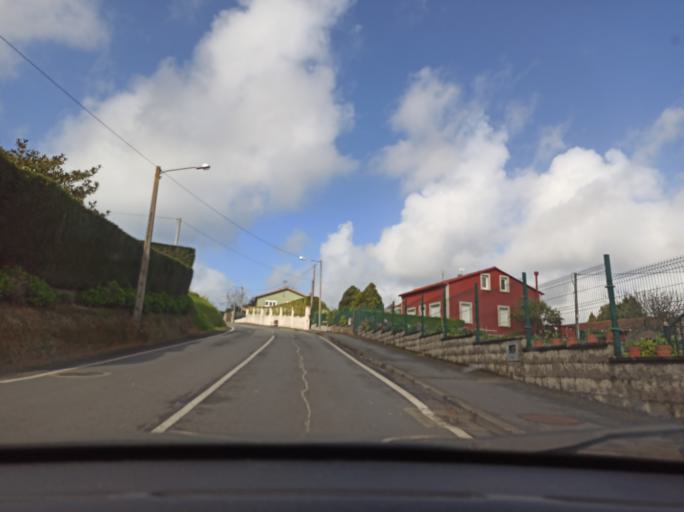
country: ES
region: Galicia
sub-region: Provincia da Coruna
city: Cambre
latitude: 43.3257
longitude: -8.3536
